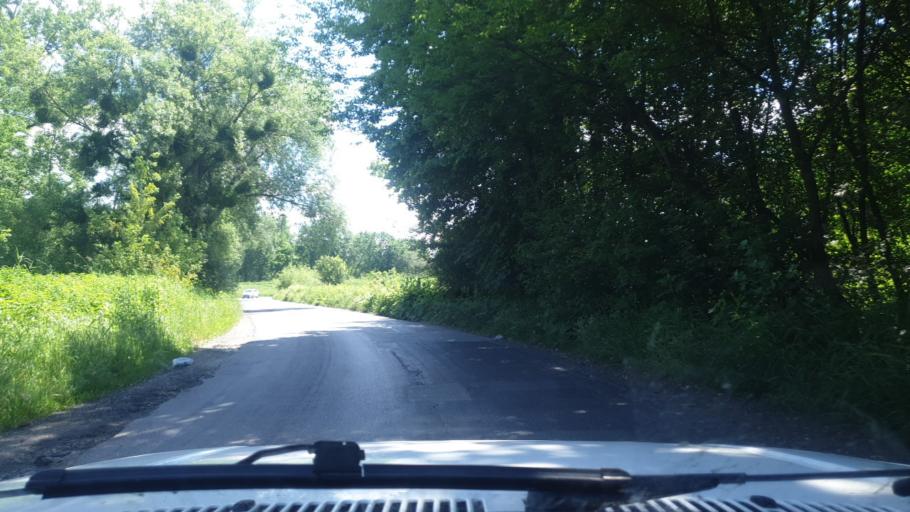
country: PL
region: Lower Silesian Voivodeship
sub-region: Powiat wroclawski
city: Radwanice
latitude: 51.0926
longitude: 17.0953
